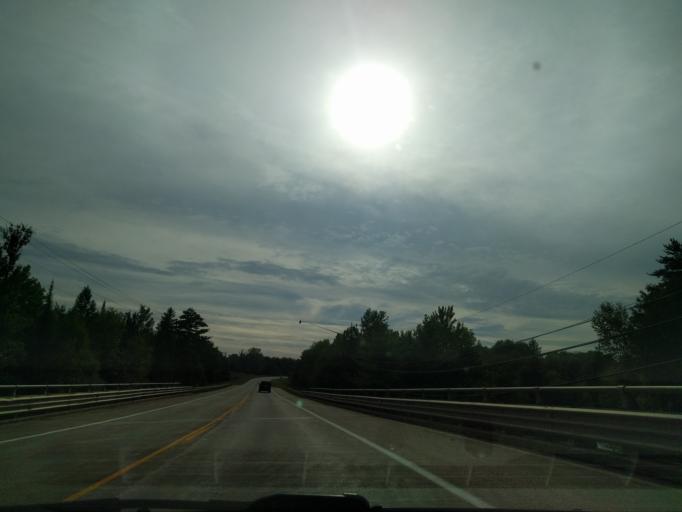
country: US
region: Michigan
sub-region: Marquette County
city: Gwinn
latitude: 46.2855
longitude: -87.4537
